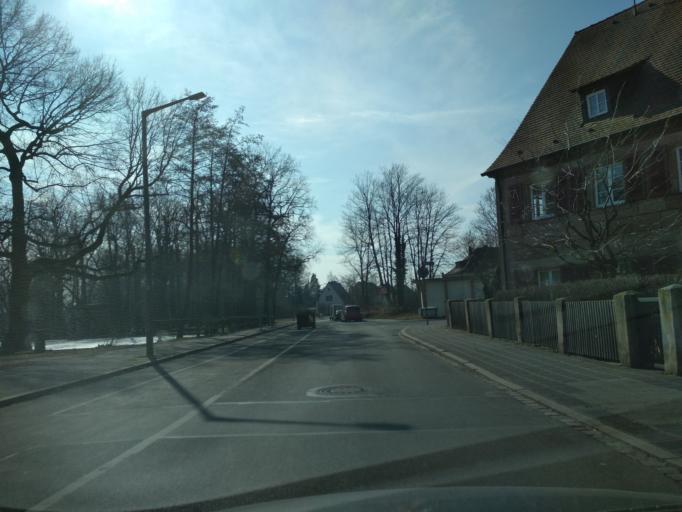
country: DE
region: Bavaria
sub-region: Regierungsbezirk Mittelfranken
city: Stein
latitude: 49.4046
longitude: 11.0415
